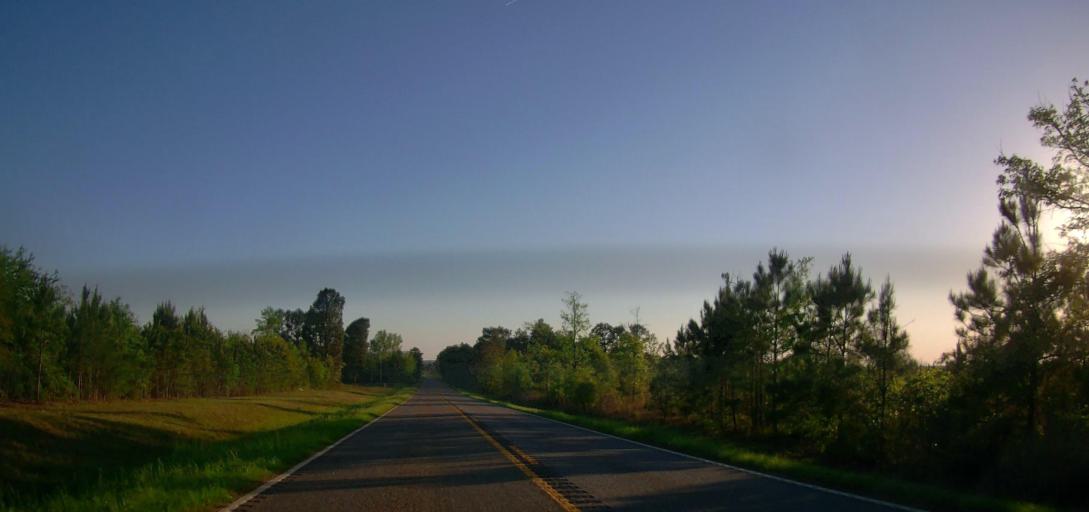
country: US
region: Georgia
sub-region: Marion County
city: Buena Vista
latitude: 32.4243
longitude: -84.4324
